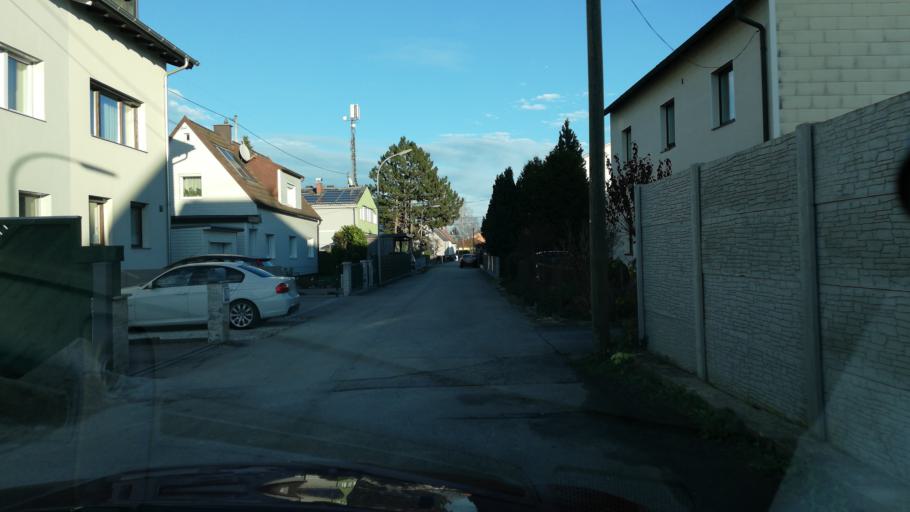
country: AT
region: Upper Austria
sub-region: Politischer Bezirk Linz-Land
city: Traun
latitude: 48.2315
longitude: 14.2461
